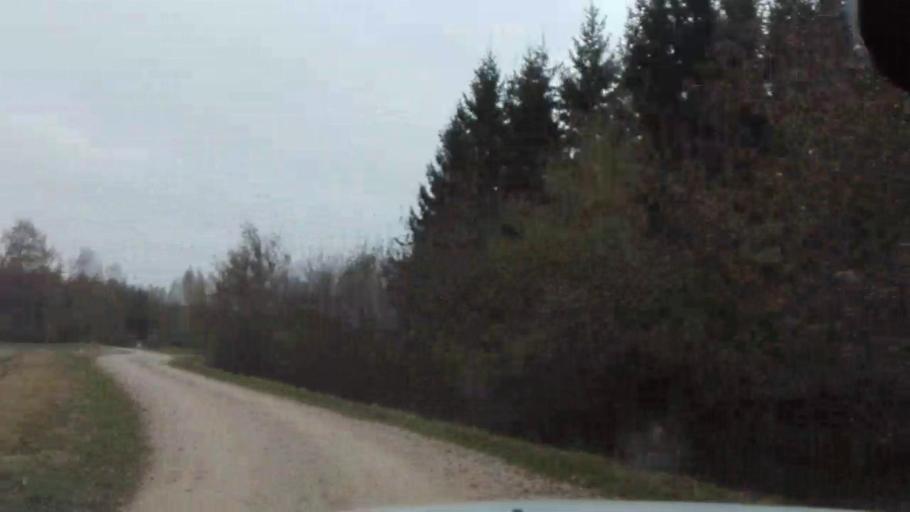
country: EE
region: Jogevamaa
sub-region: Poltsamaa linn
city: Poltsamaa
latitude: 58.5062
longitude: 25.9686
